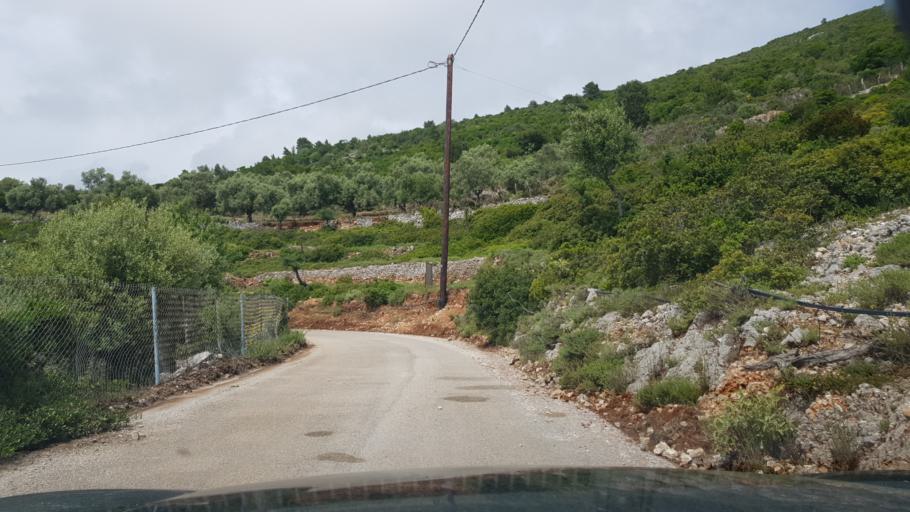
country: GR
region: Ionian Islands
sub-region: Lefkada
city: Nidri
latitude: 38.6173
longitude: 20.5658
